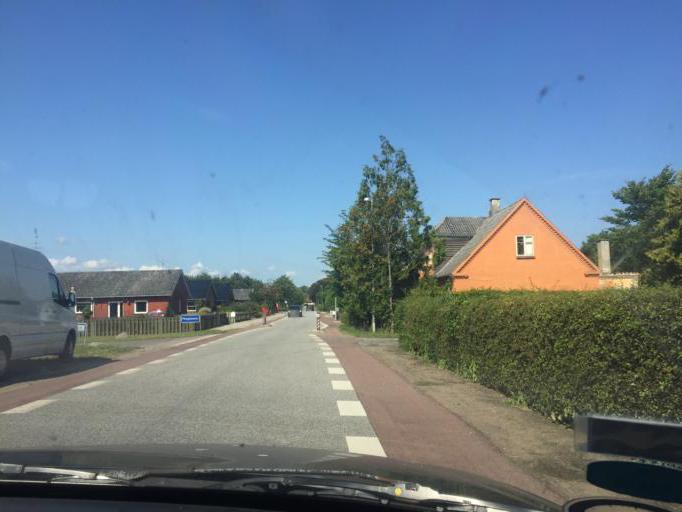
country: DK
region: Zealand
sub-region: Lolland Kommune
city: Maribo
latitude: 54.7984
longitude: 11.5130
